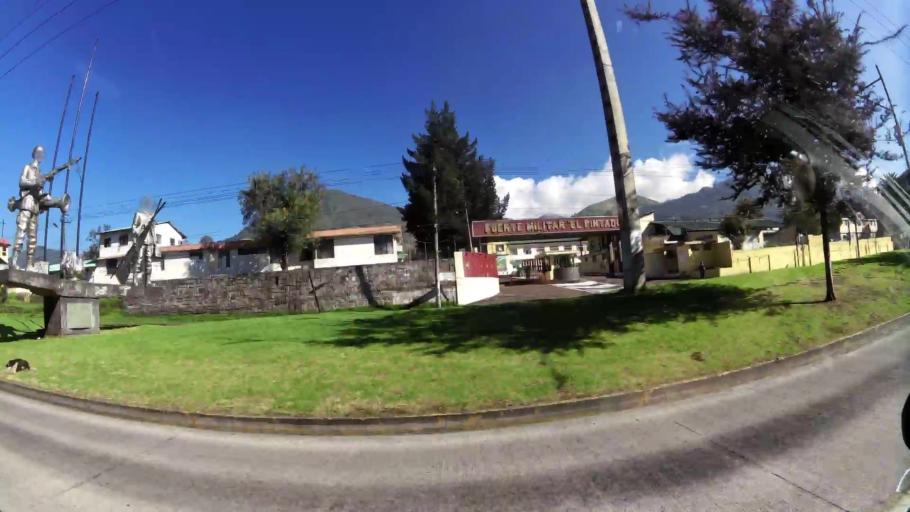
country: EC
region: Pichincha
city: Quito
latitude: -0.2478
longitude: -78.5354
